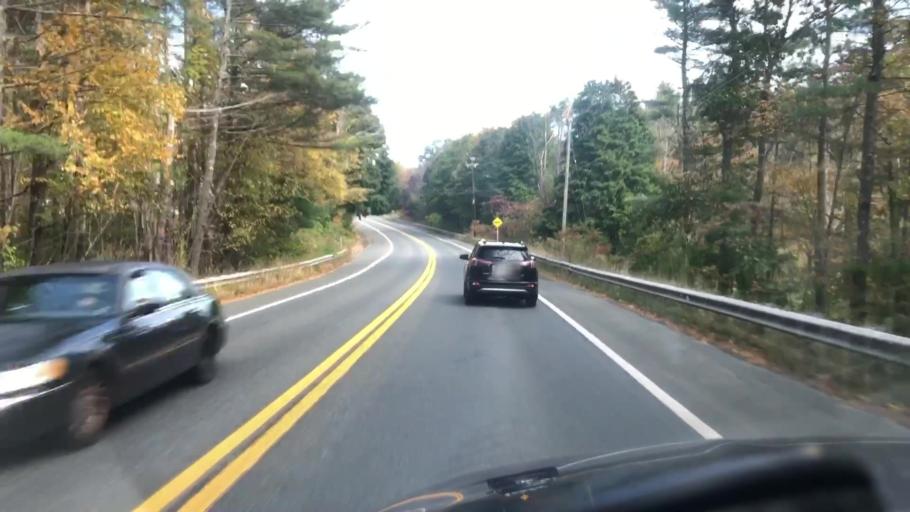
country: US
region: Massachusetts
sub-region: Franklin County
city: Shelburne
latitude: 42.5898
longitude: -72.6896
